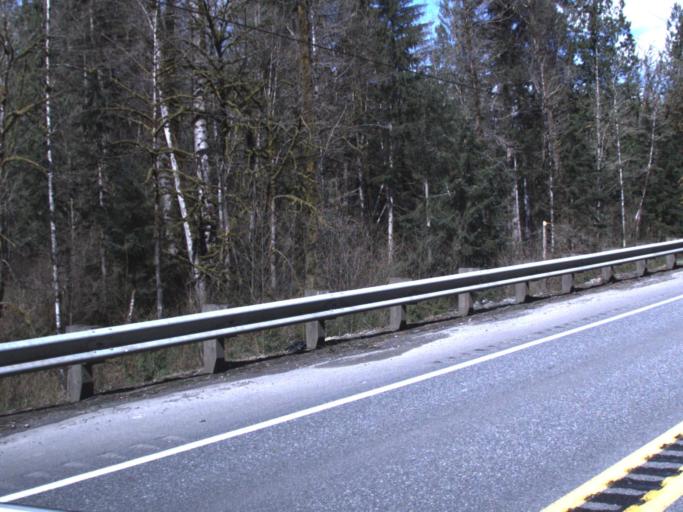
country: US
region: Washington
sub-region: King County
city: Black Diamond
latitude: 47.2754
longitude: -121.9922
